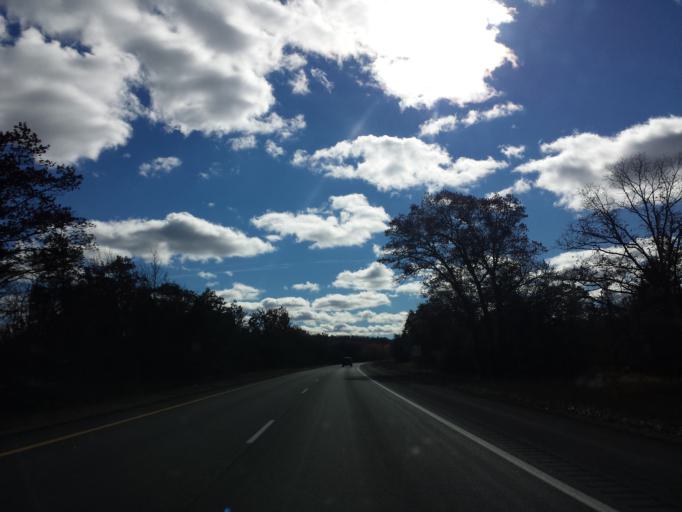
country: US
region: Michigan
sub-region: Cheboygan County
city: Indian River
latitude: 45.3749
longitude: -84.6076
